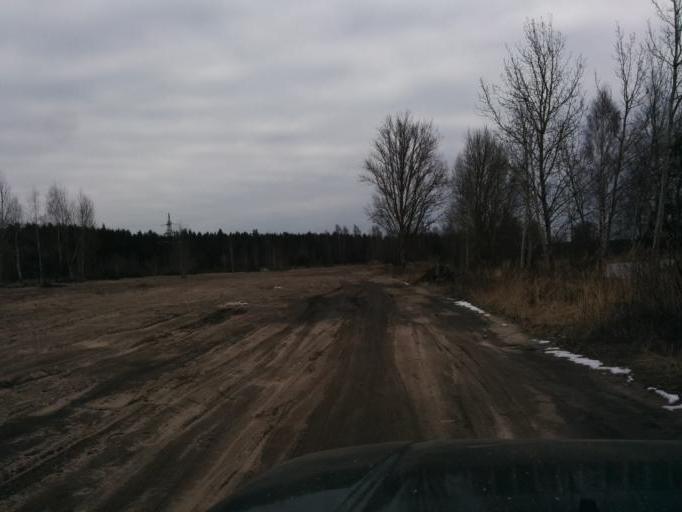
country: LV
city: Tireli
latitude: 56.9406
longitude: 23.6425
